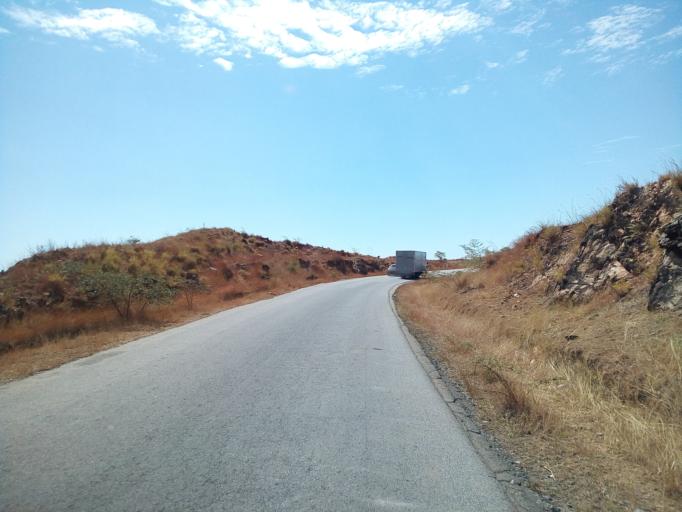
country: MG
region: Betsiboka
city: Maevatanana
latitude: -16.9453
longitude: 46.8550
